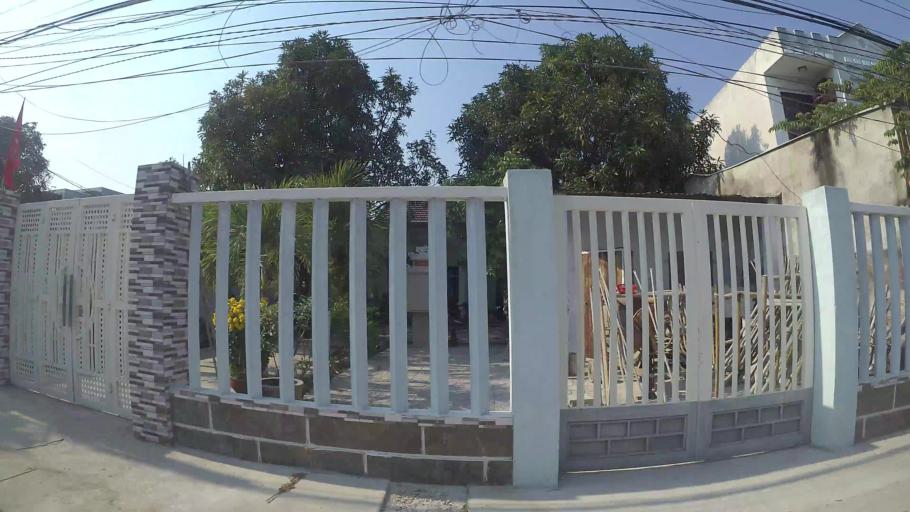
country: VN
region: Da Nang
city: Ngu Hanh Son
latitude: 15.9582
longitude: 108.2608
